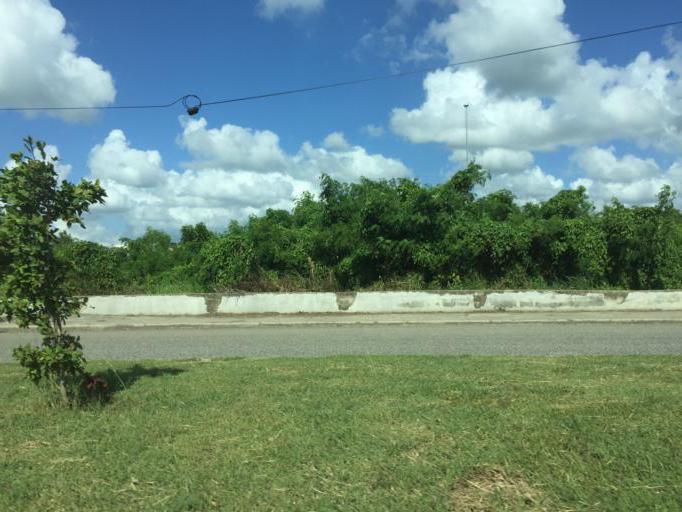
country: DO
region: Santo Domingo
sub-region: Santo Domingo
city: Boca Chica
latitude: 18.4601
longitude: -69.6595
